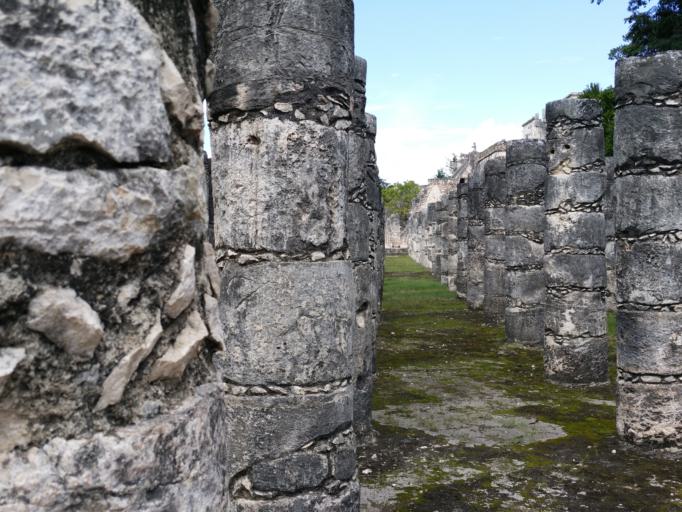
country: MX
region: Yucatan
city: Chichen-Itza
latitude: 20.6825
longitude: -88.5676
